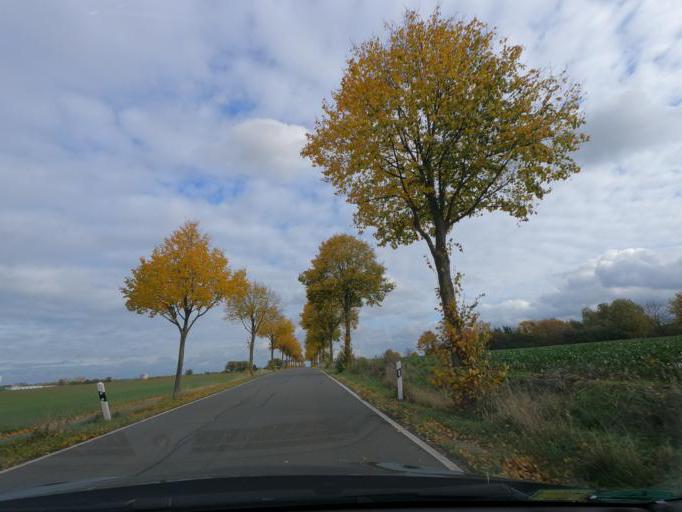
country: DE
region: Lower Saxony
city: Leiferde
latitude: 52.1997
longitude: 10.4875
